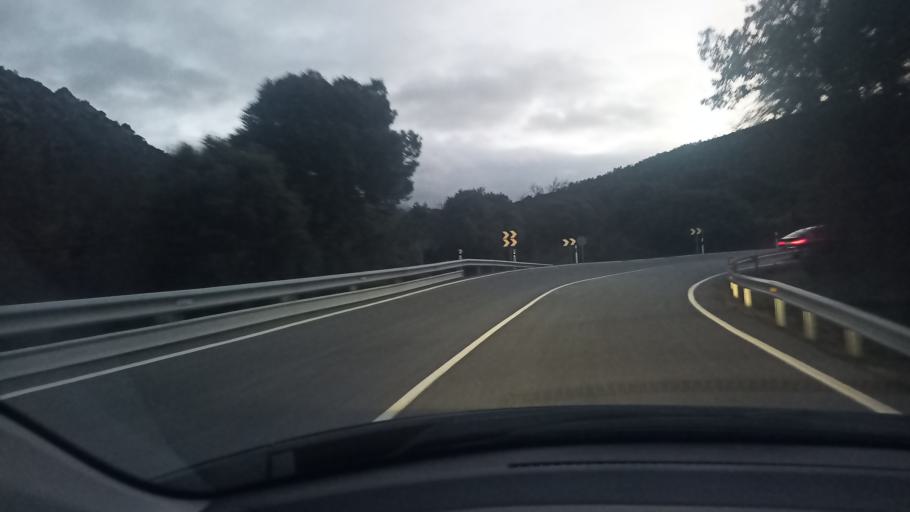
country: ES
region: Madrid
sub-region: Provincia de Madrid
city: Robledo de Chavela
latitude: 40.4608
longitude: -4.2609
